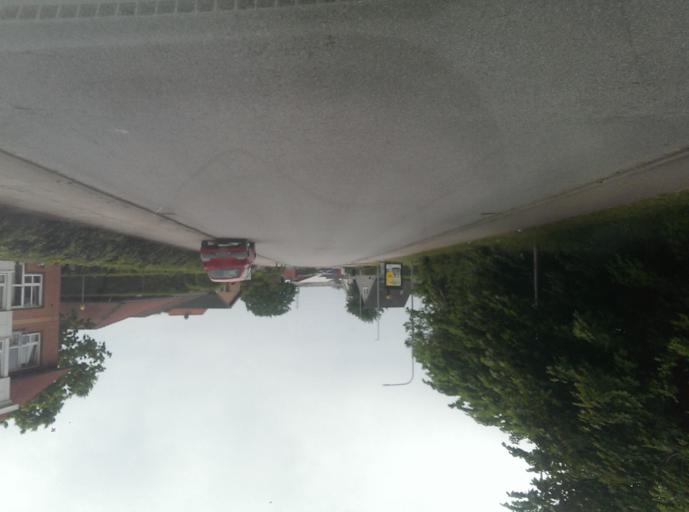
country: DK
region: South Denmark
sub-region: Esbjerg Kommune
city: Esbjerg
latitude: 55.4662
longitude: 8.4867
